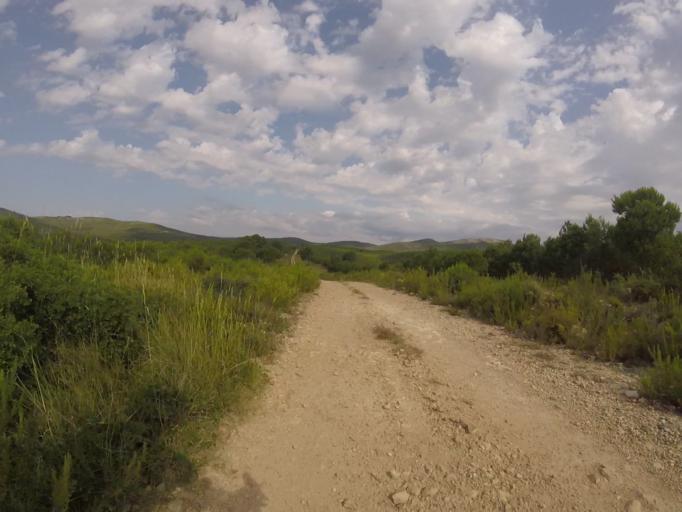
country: ES
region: Valencia
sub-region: Provincia de Castello
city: Alcala de Xivert
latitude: 40.3617
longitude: 0.2012
